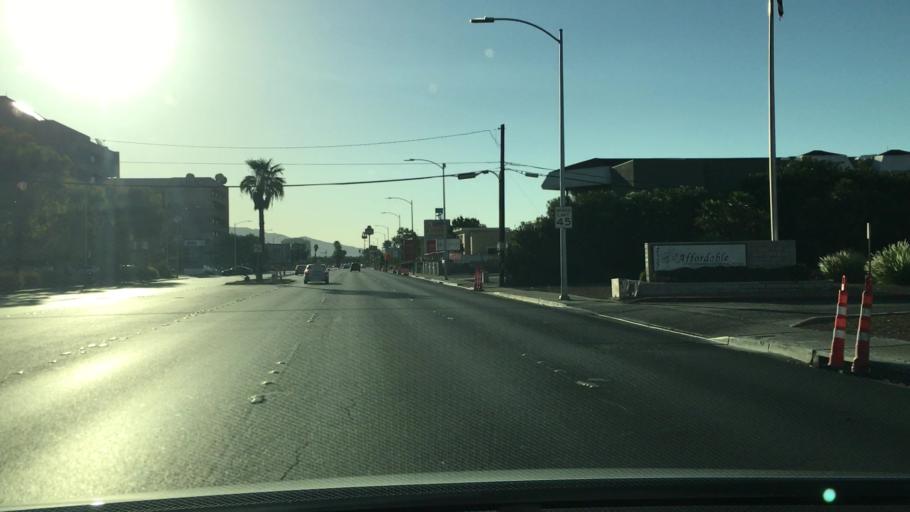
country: US
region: Nevada
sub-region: Clark County
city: Las Vegas
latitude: 36.1588
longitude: -115.1715
